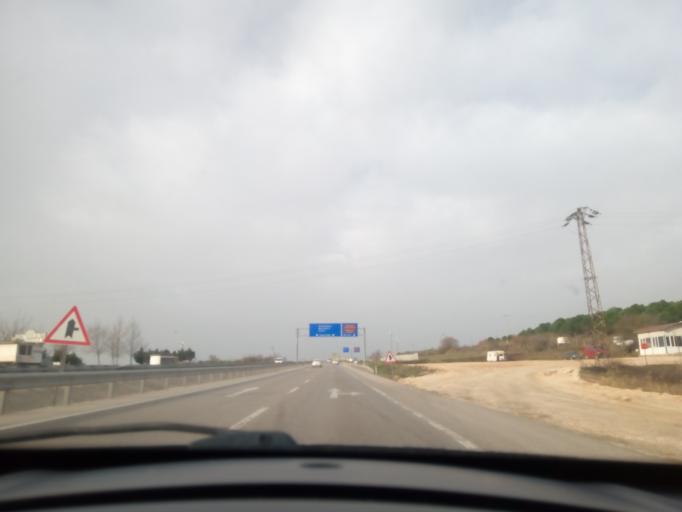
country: TR
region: Bursa
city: Mahmudiye
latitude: 40.2128
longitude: 28.6909
